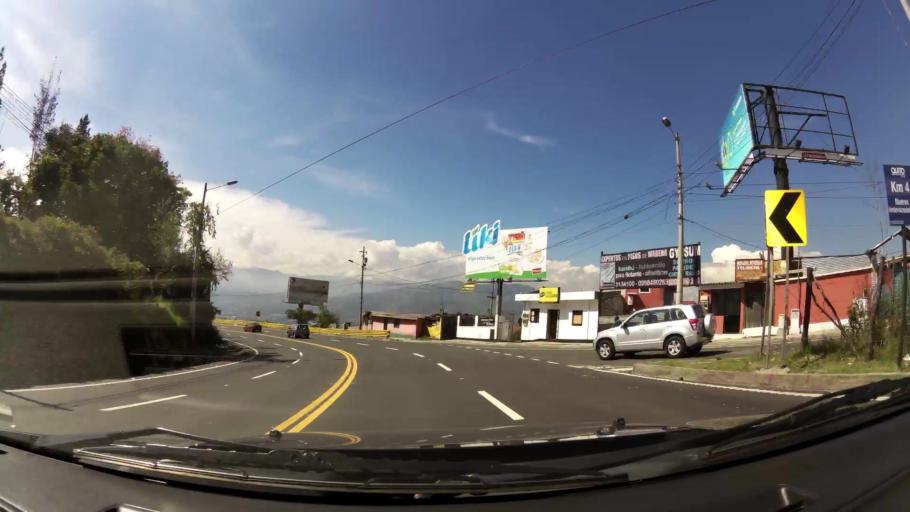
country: EC
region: Pichincha
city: Quito
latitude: -0.1926
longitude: -78.4534
